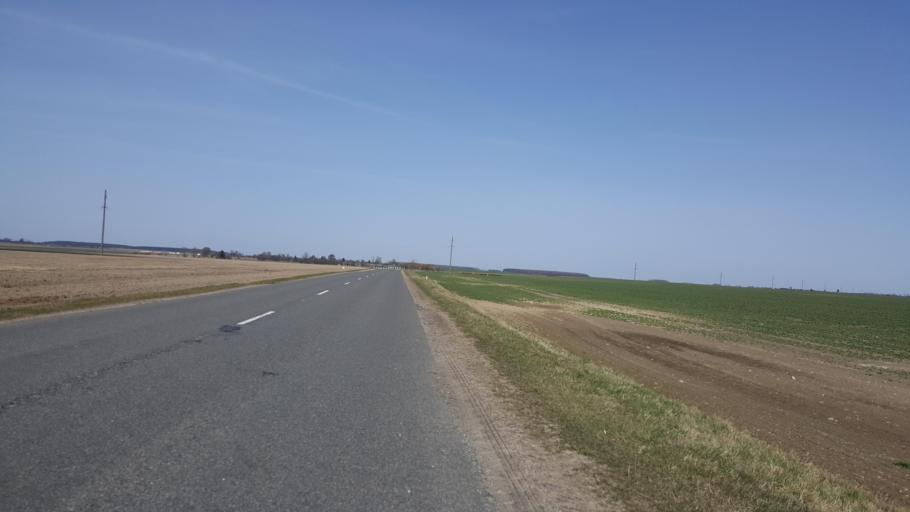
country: BY
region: Brest
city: Kamyanyets
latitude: 52.4179
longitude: 23.7803
